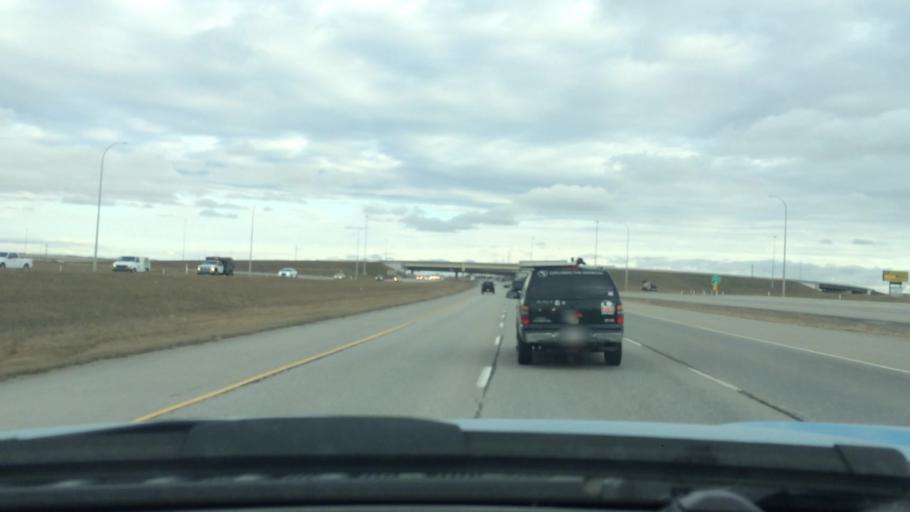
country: CA
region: Alberta
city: Airdrie
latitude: 51.1687
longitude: -114.0013
